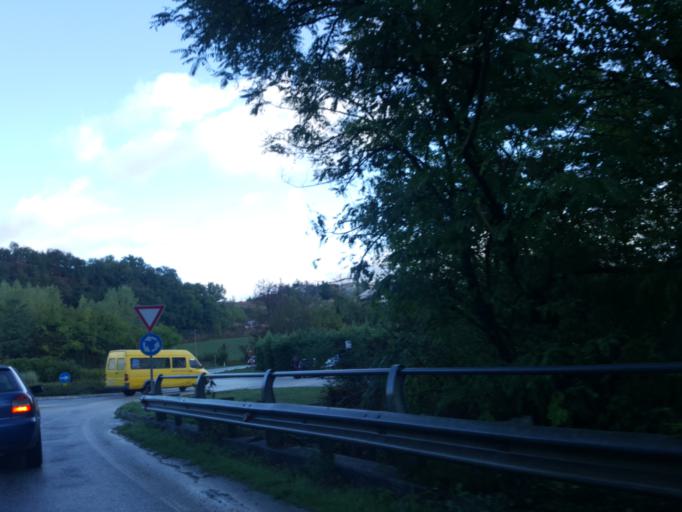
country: IT
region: The Marches
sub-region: Provincia di Macerata
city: Castelraimondo
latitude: 43.1965
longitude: 13.0504
